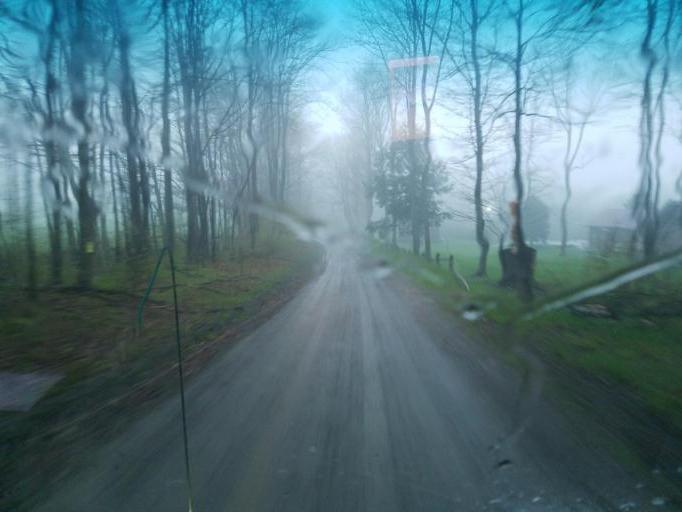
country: US
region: Pennsylvania
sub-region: Tioga County
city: Westfield
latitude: 41.9330
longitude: -77.7152
